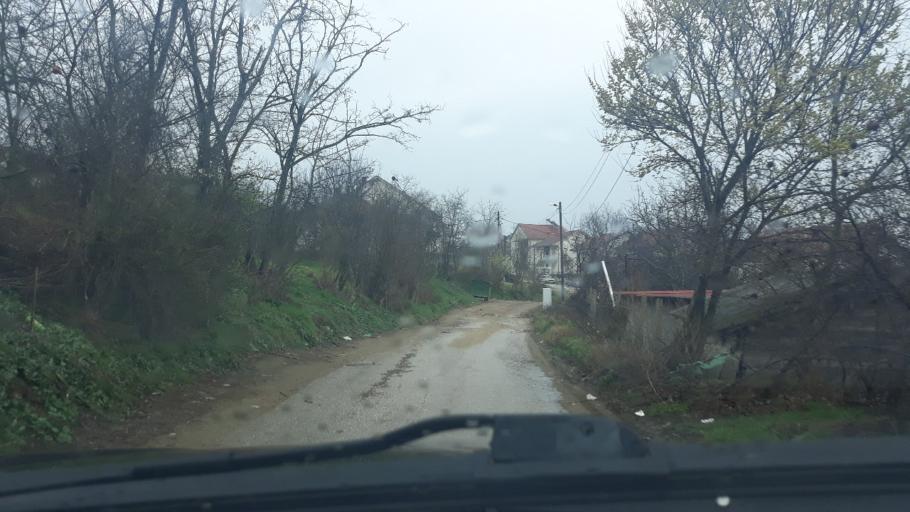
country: MK
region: Valandovo
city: Valandovo
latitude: 41.3174
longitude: 22.5521
